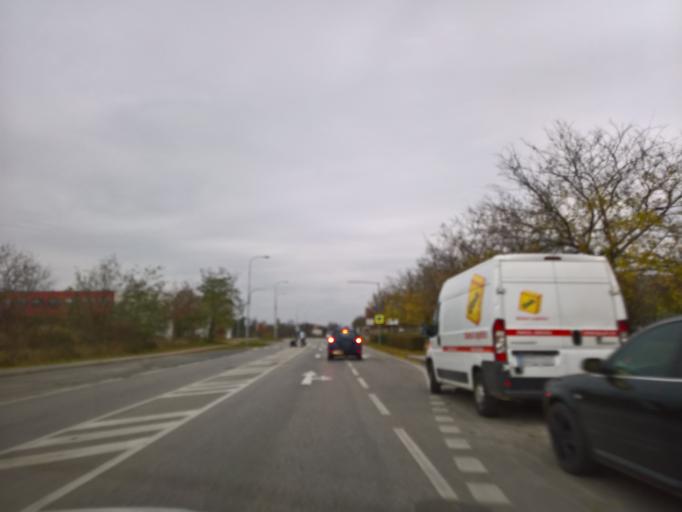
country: SK
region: Nitriansky
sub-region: Okres Nitra
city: Nitra
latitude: 48.2994
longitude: 18.0661
